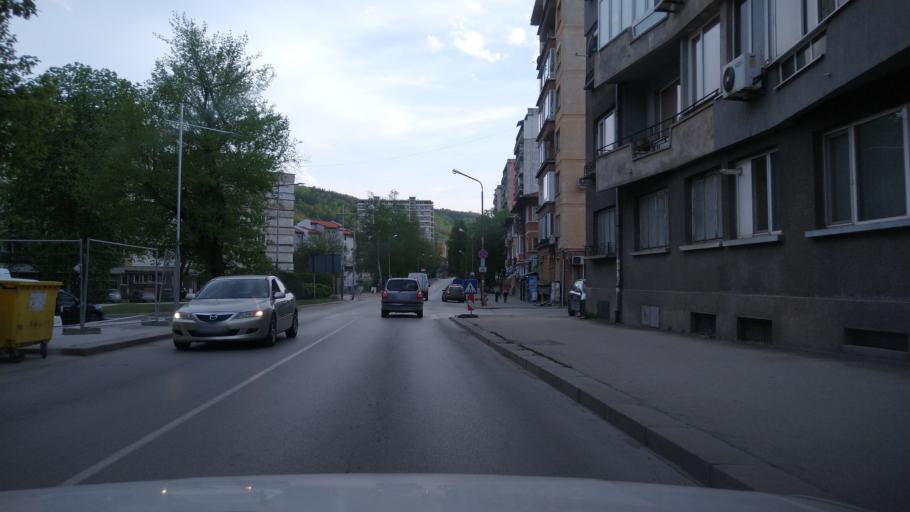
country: BG
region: Gabrovo
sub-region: Obshtina Gabrovo
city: Gabrovo
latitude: 42.8736
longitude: 25.3158
